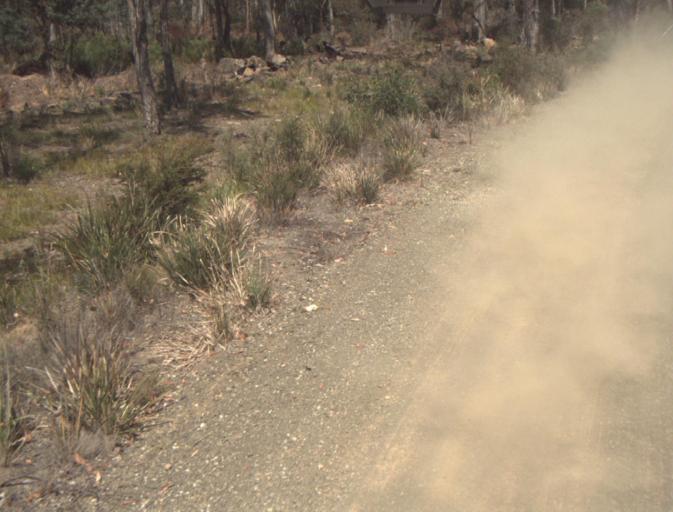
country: AU
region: Tasmania
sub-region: Launceston
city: Mayfield
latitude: -41.2774
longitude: 147.0984
